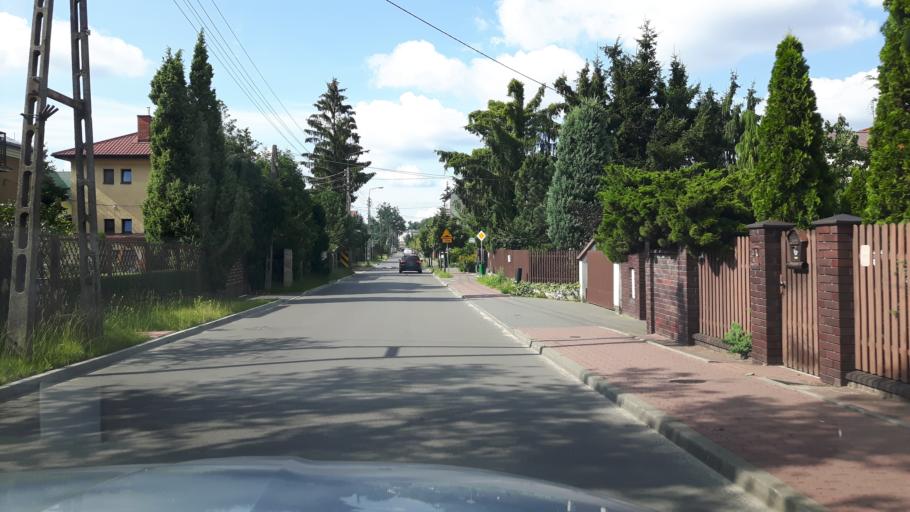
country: PL
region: Masovian Voivodeship
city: Zielonka
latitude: 52.2981
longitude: 21.1586
